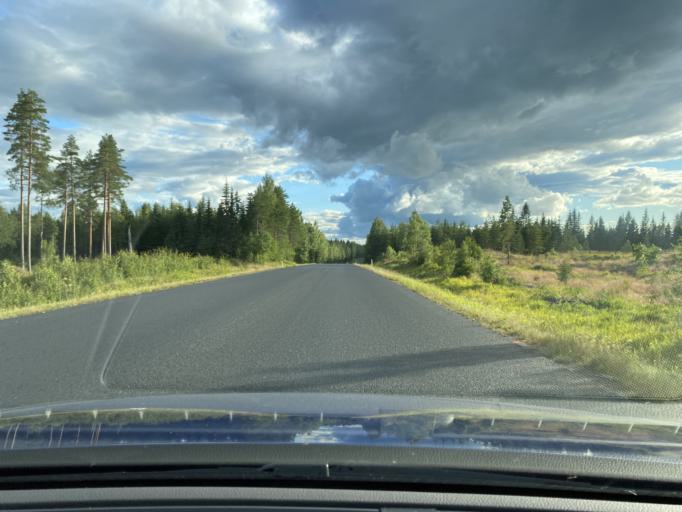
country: FI
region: Haeme
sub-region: Haemeenlinna
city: Renko
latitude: 60.9120
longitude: 24.3178
